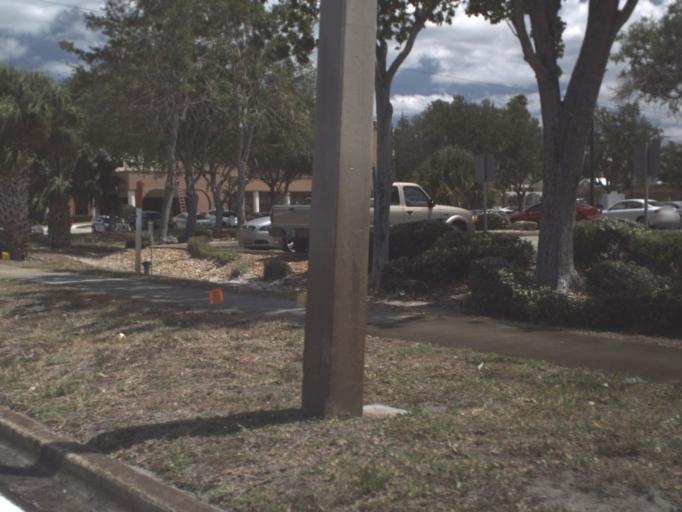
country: US
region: Florida
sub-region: Brevard County
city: Melbourne
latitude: 28.0933
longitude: -80.6181
